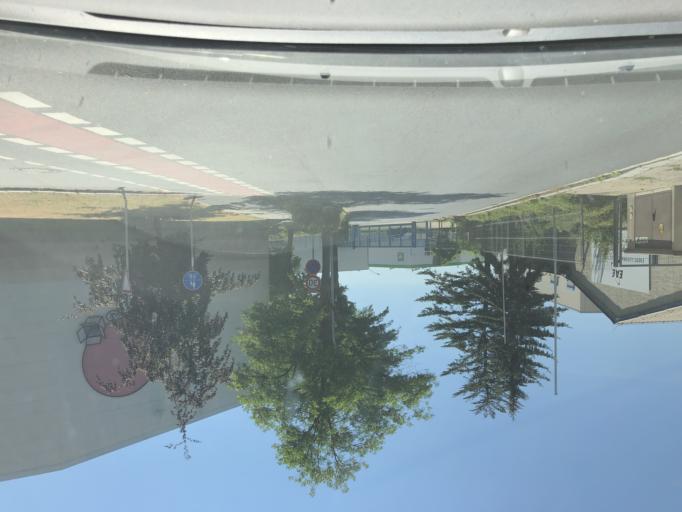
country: DE
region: Saxony
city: Coswig
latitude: 51.1189
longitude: 13.5877
